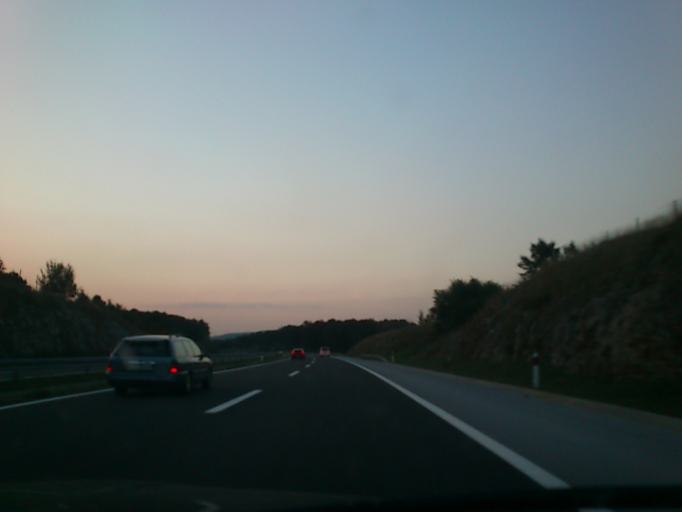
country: HR
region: Karlovacka
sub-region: Grad Ogulin
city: Ogulin
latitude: 45.3533
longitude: 15.2779
